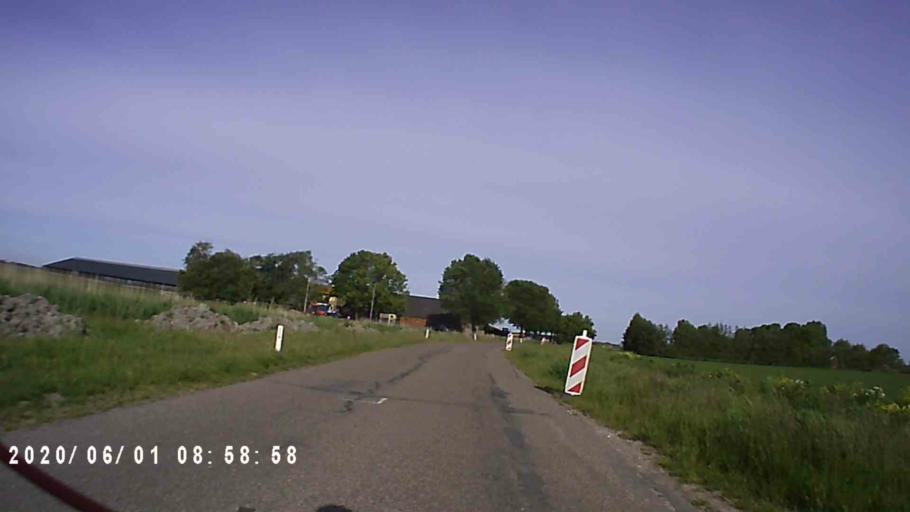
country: NL
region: Friesland
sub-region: Gemeente Ferwerderadiel
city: Hallum
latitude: 53.2822
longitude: 5.8017
